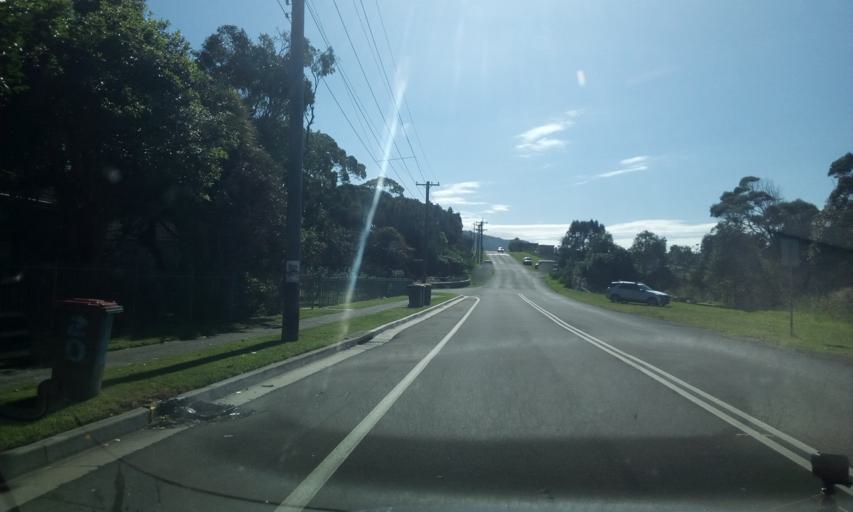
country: AU
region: New South Wales
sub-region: Wollongong
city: Bulli
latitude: -34.3431
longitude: 150.9199
